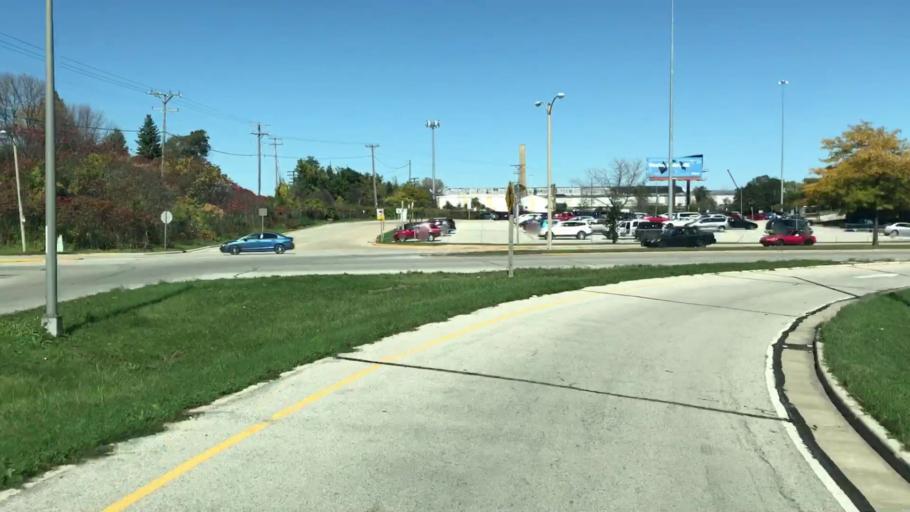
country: US
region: Wisconsin
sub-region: Milwaukee County
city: Saint Francis
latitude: 42.9813
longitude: -87.9181
